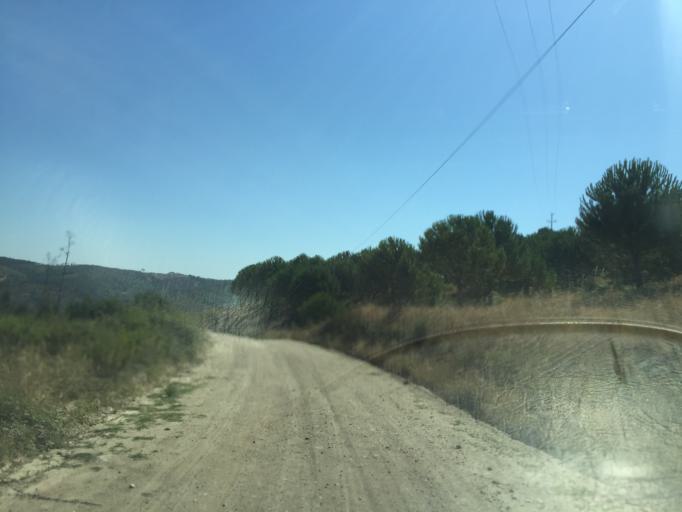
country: PT
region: Santarem
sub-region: Constancia
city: Constancia
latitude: 39.5413
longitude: -8.2838
